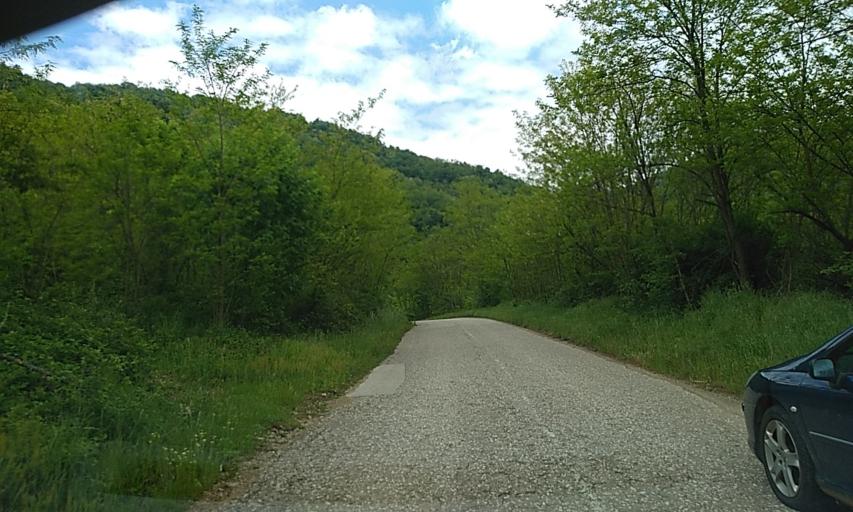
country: RS
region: Central Serbia
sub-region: Pcinjski Okrug
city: Vladicin Han
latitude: 42.7515
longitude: 22.0610
